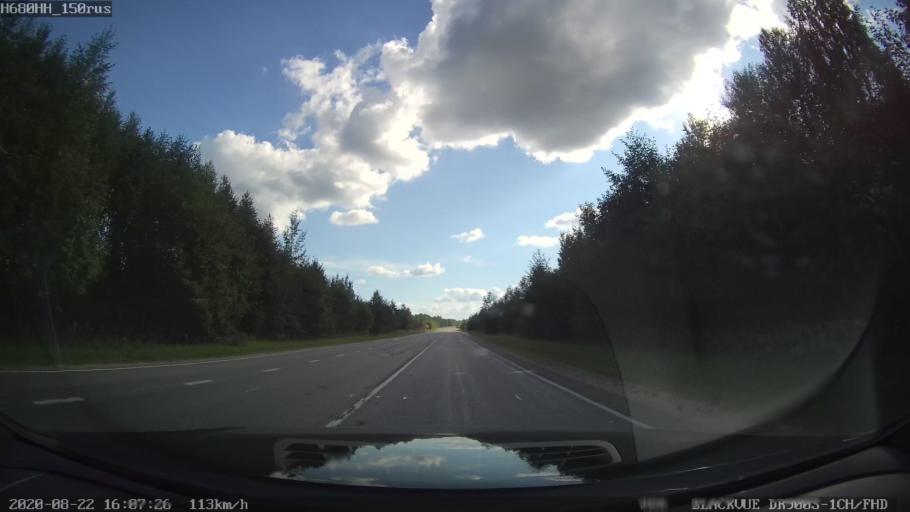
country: RU
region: Tverskaya
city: Rameshki
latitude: 57.5526
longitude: 36.3131
